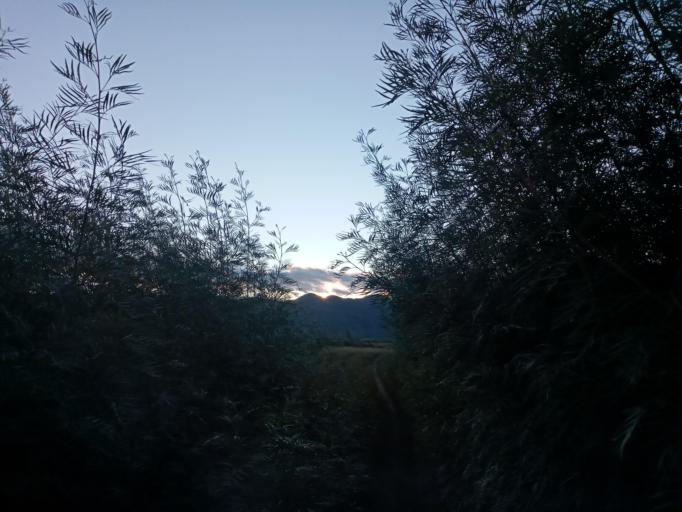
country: MG
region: Anosy
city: Fort Dauphin
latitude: -24.5119
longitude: 47.2269
